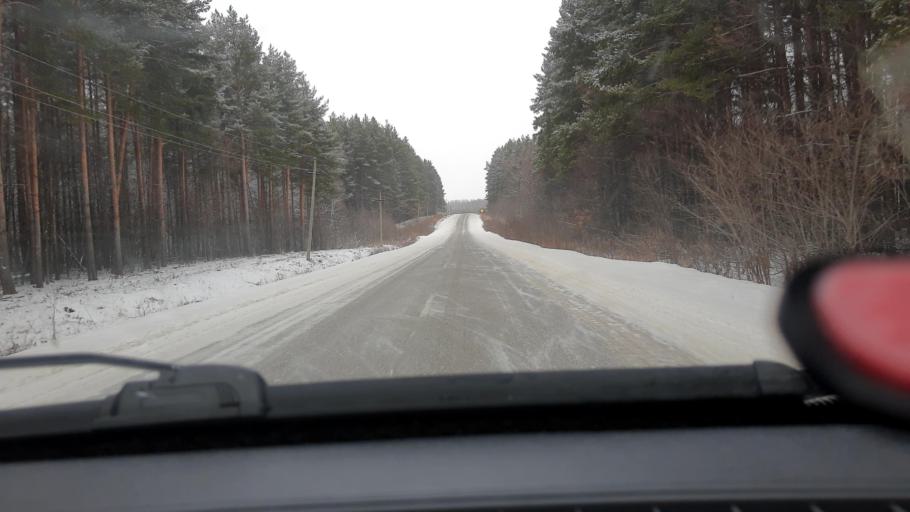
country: RU
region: Bashkortostan
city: Iglino
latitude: 54.6748
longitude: 56.4192
